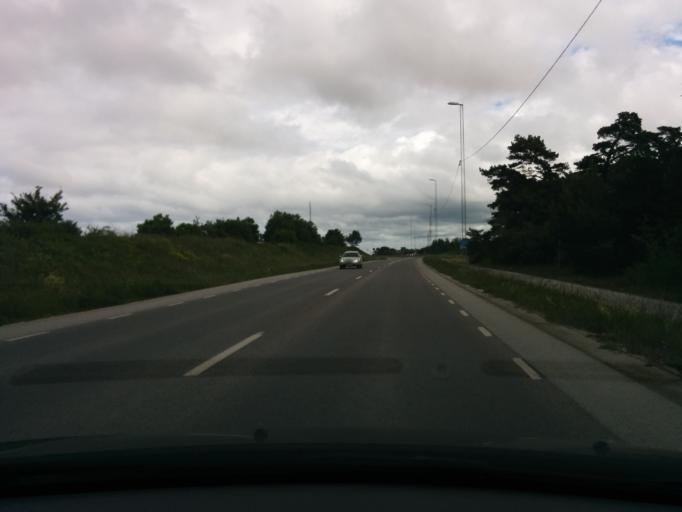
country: SE
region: Gotland
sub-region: Gotland
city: Visby
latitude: 57.6304
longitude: 18.3256
